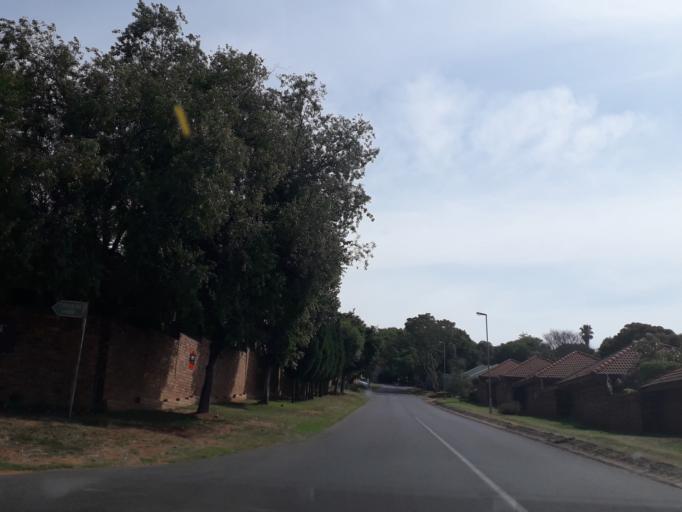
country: ZA
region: Gauteng
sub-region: City of Johannesburg Metropolitan Municipality
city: Roodepoort
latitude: -26.0730
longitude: 27.9573
